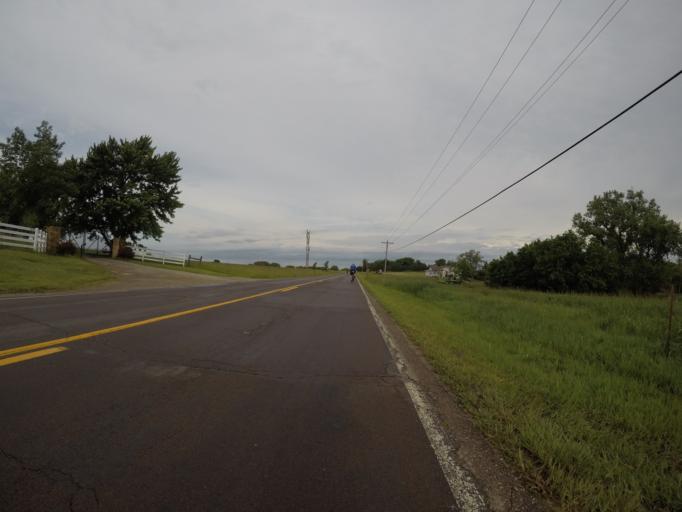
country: US
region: Kansas
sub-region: Shawnee County
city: Auburn
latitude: 38.9562
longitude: -95.8016
